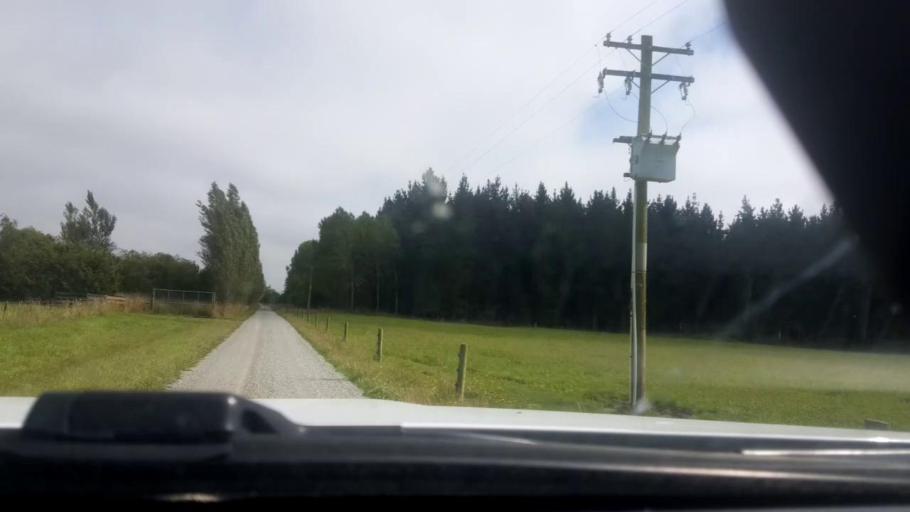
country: NZ
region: Canterbury
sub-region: Timaru District
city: Timaru
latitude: -44.3288
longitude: 171.1976
